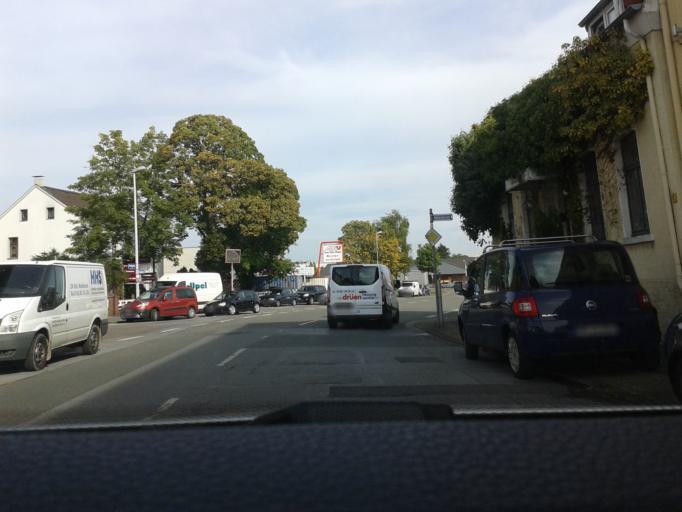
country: DE
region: North Rhine-Westphalia
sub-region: Regierungsbezirk Dusseldorf
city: Muelheim (Ruhr)
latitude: 51.4314
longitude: 6.8442
